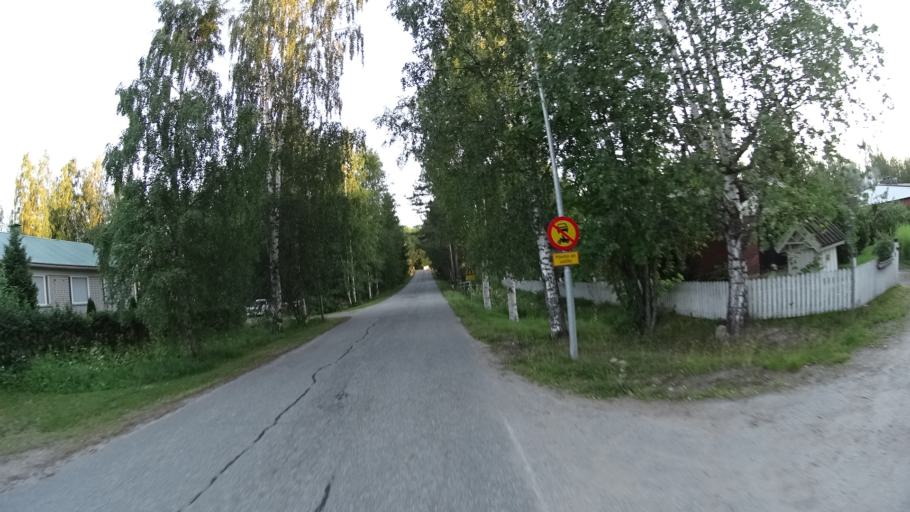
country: FI
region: Central Finland
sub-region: Jyvaeskylae
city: Petaejaevesi
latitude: 62.2542
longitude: 25.1806
